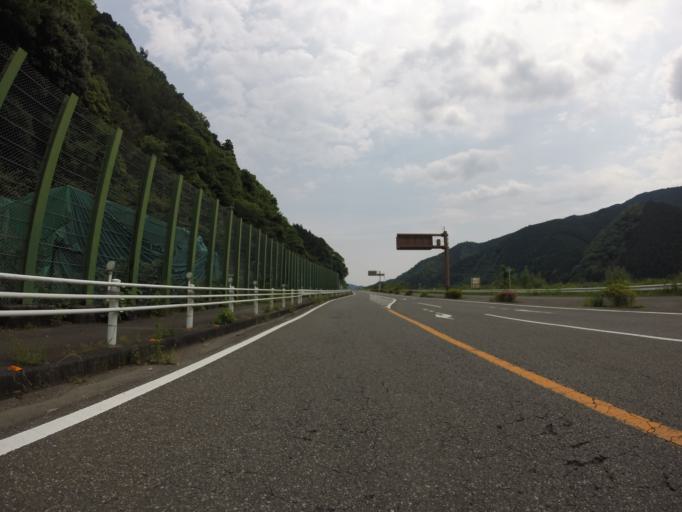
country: JP
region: Shizuoka
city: Shizuoka-shi
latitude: 35.1059
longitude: 138.3662
